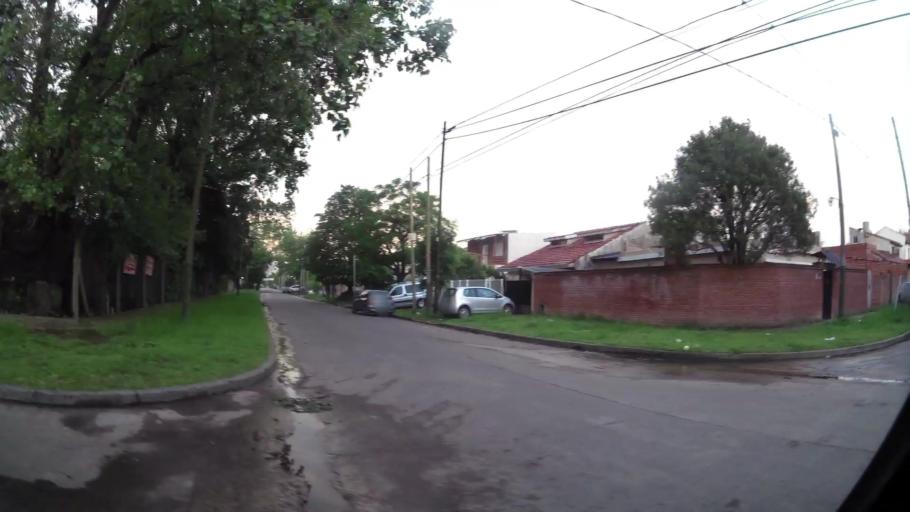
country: AR
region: Buenos Aires
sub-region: Partido de Lomas de Zamora
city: Lomas de Zamora
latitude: -34.7624
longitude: -58.3721
